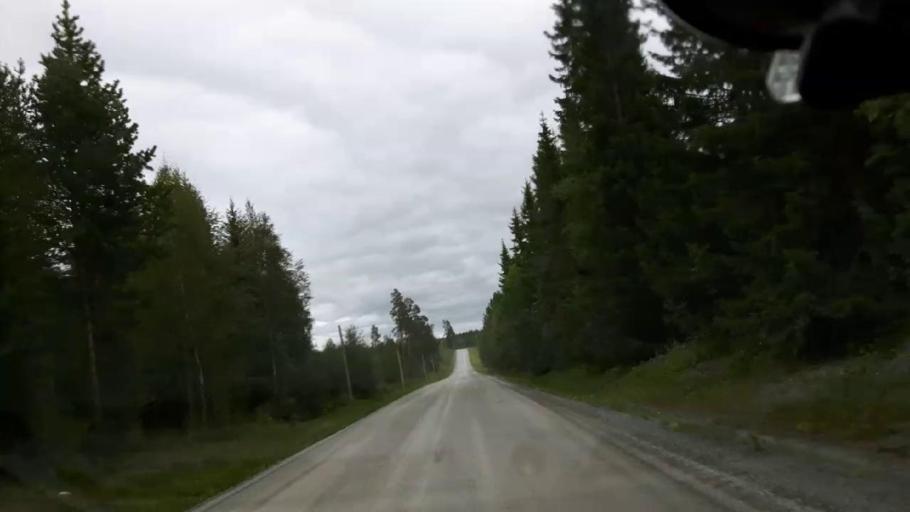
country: SE
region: Jaemtland
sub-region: OEstersunds Kommun
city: Brunflo
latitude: 63.0968
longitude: 15.1274
